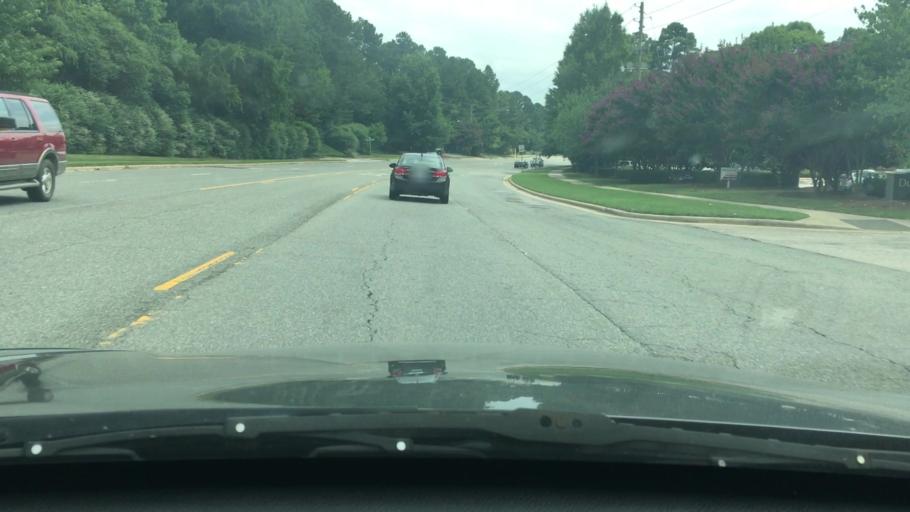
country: US
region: North Carolina
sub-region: Wake County
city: West Raleigh
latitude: 35.8553
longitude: -78.7118
